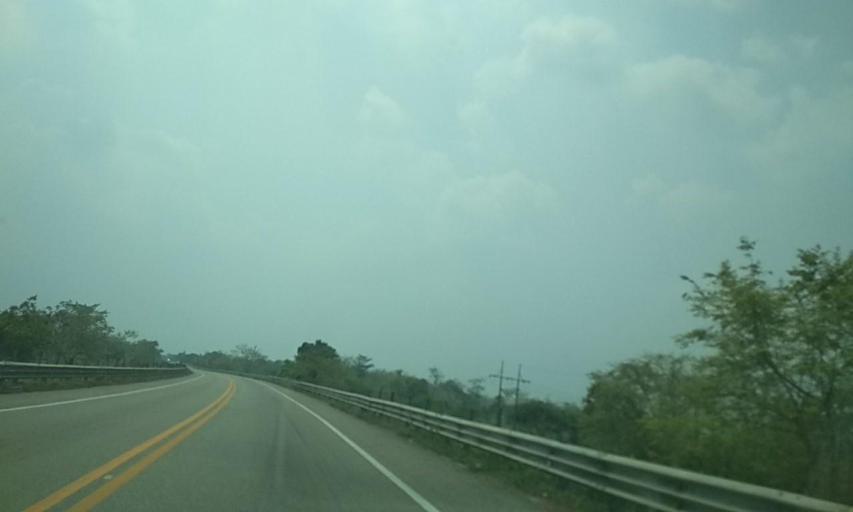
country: MX
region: Tabasco
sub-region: Huimanguillo
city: Francisco Rueda
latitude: 17.7611
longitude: -94.0098
